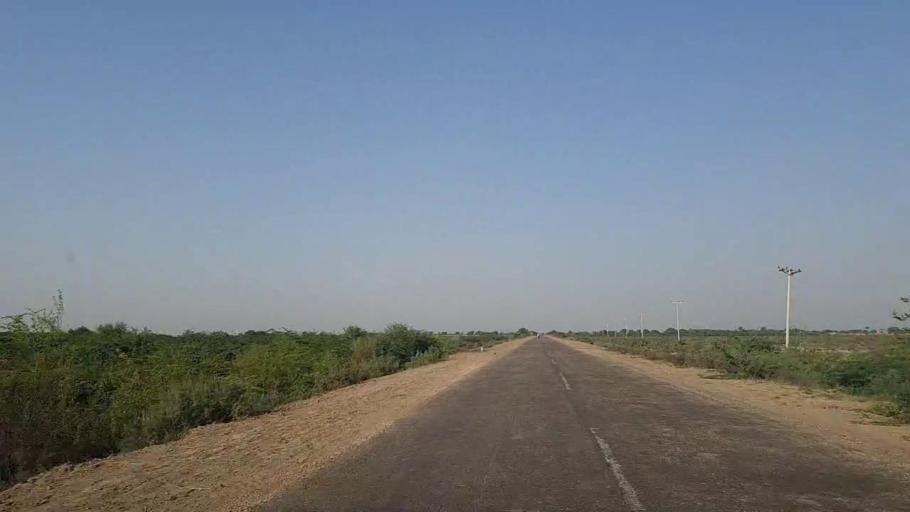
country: PK
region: Sindh
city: Mirpur Batoro
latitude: 24.6161
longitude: 68.4049
